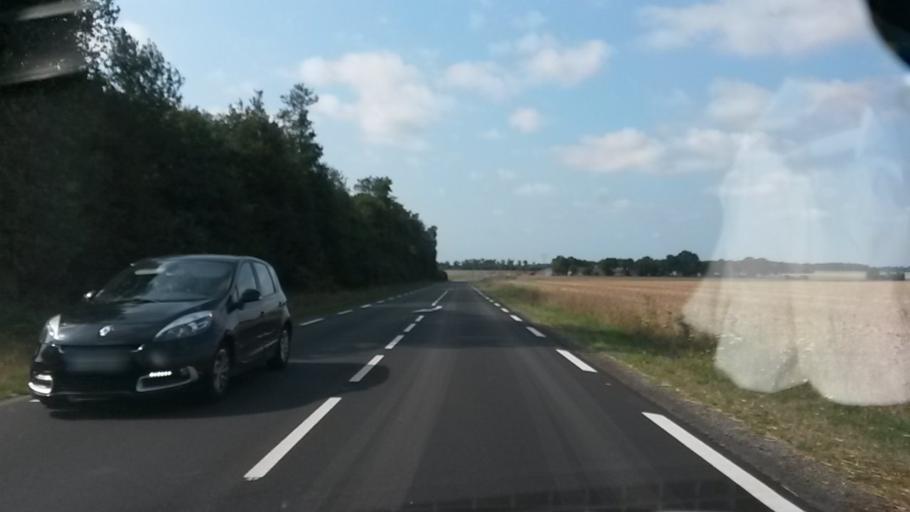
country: FR
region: Haute-Normandie
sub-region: Departement de l'Eure
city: Tillieres-sur-Avre
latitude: 48.7947
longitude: 0.9922
